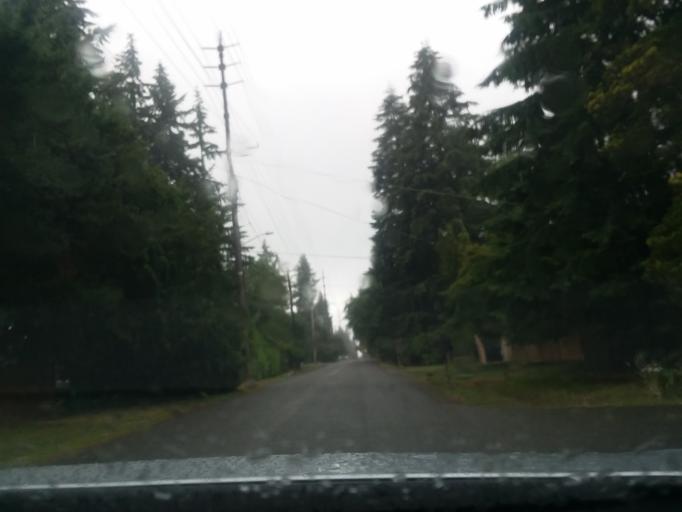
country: US
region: Washington
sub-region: King County
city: Shoreline
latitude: 47.7162
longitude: -122.3208
